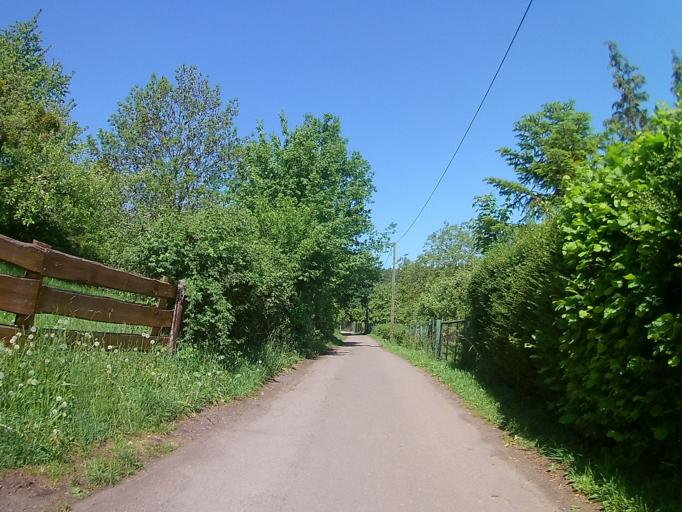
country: DE
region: Baden-Wuerttemberg
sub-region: Regierungsbezirk Stuttgart
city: Leinfelden-Echterdingen
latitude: 48.7412
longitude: 9.1166
